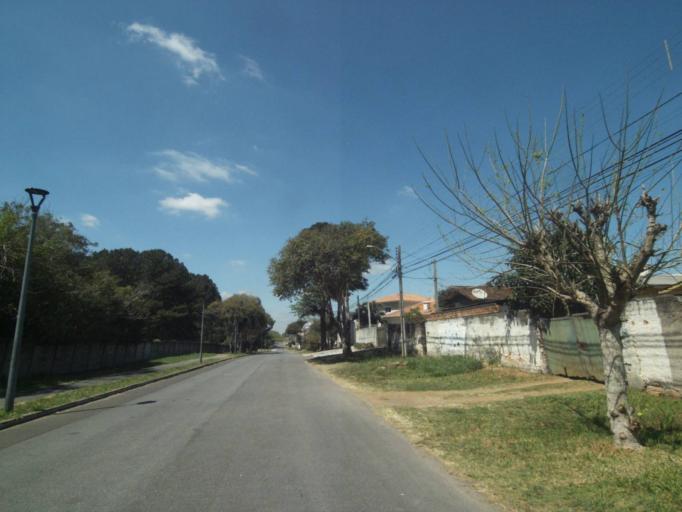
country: BR
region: Parana
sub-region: Sao Jose Dos Pinhais
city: Sao Jose dos Pinhais
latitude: -25.5106
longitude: -49.2386
